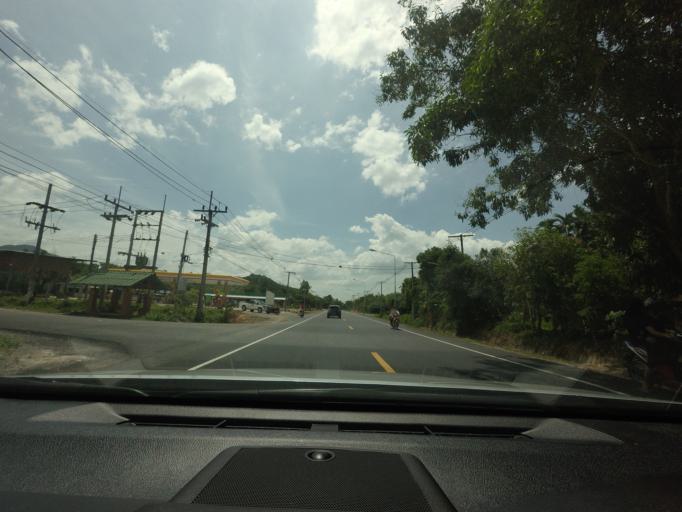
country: TH
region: Yala
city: Krong Pi Nang
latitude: 6.4656
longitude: 101.3282
